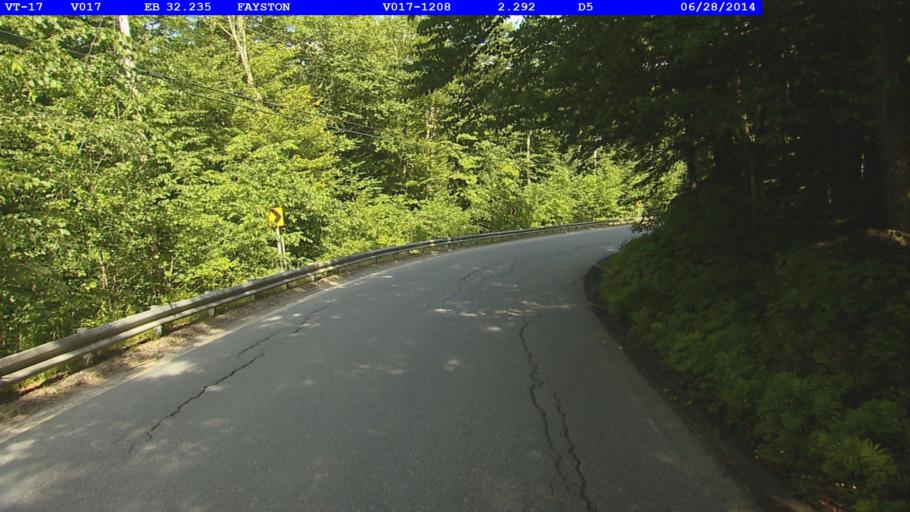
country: US
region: Vermont
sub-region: Addison County
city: Bristol
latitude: 44.2040
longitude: -72.8978
